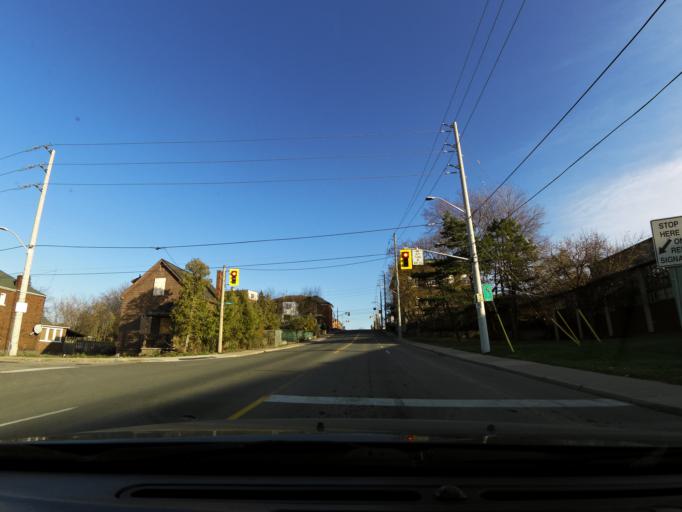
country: CA
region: Ontario
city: Hamilton
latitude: 43.2655
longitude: -79.8714
